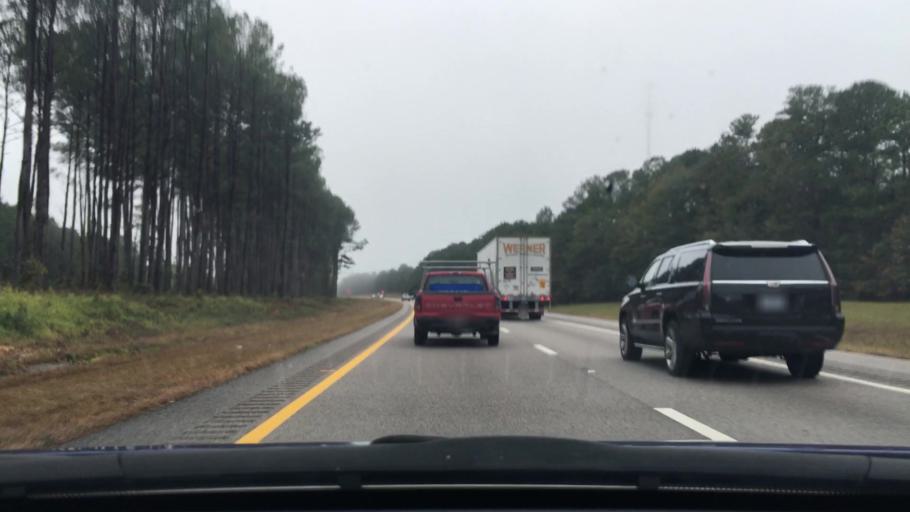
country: US
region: South Carolina
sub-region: Kershaw County
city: Camden
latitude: 34.2153
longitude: -80.5072
